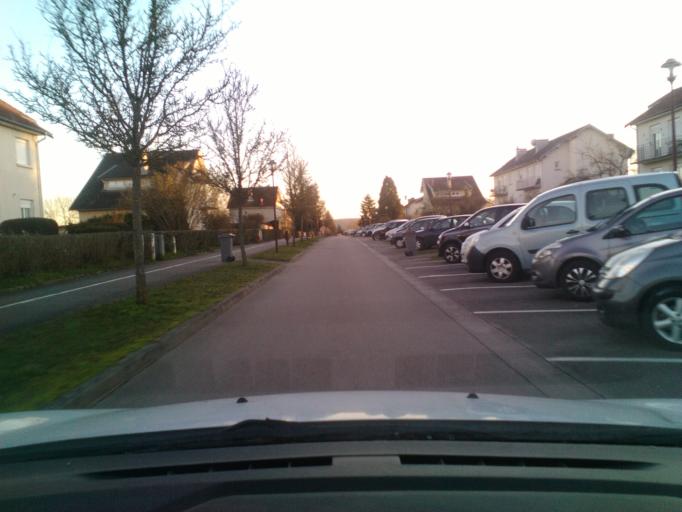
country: FR
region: Lorraine
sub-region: Departement des Vosges
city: Mirecourt
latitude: 48.2950
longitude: 6.1262
